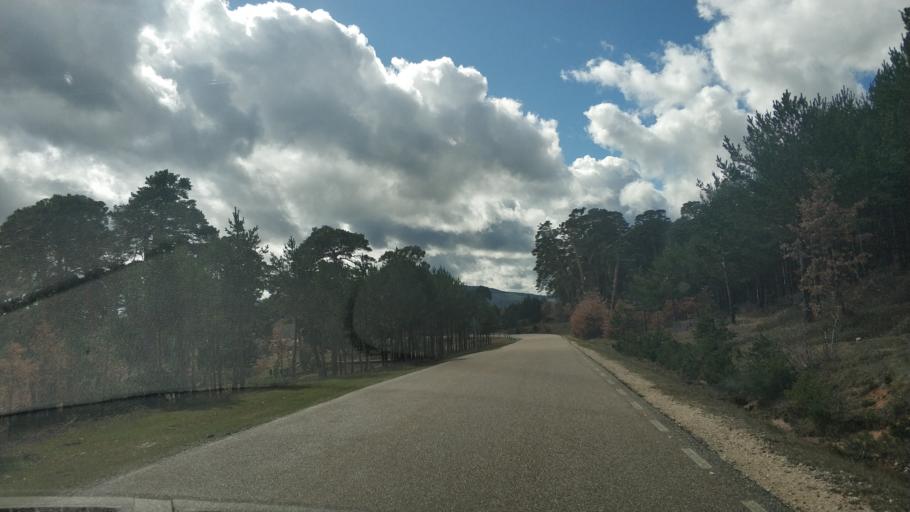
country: ES
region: Castille and Leon
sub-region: Provincia de Burgos
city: Quintanar de la Sierra
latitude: 41.9903
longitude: -3.0269
